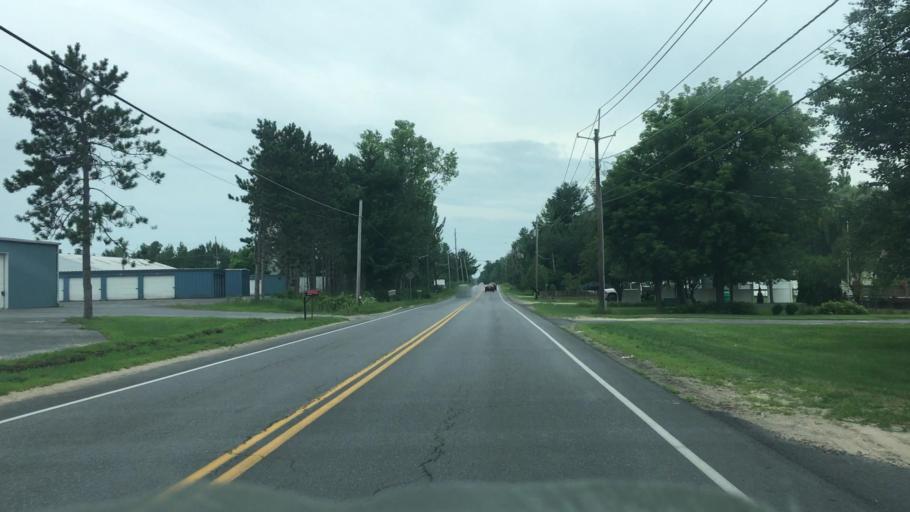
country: US
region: New York
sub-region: Clinton County
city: Plattsburgh West
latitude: 44.6657
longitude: -73.5080
